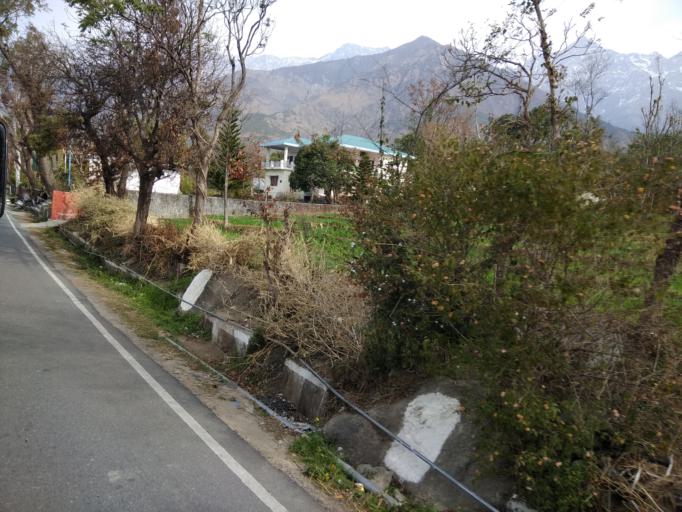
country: IN
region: Himachal Pradesh
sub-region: Kangra
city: Dharmsala
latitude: 32.1687
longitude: 76.3911
